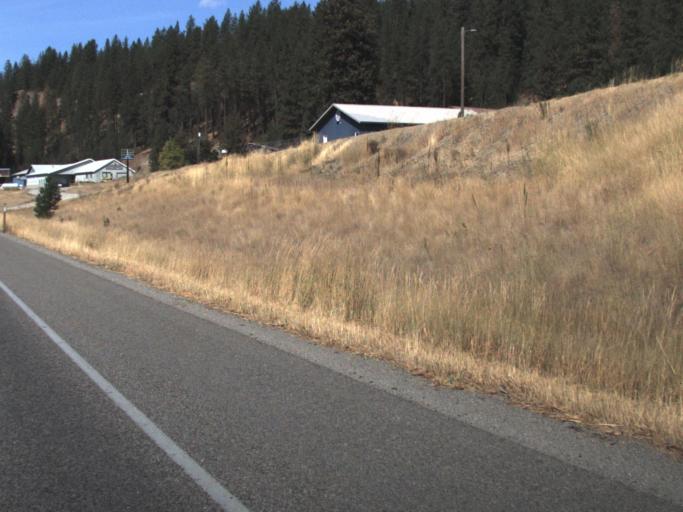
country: US
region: Washington
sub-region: Stevens County
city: Chewelah
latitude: 48.3002
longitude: -117.7616
